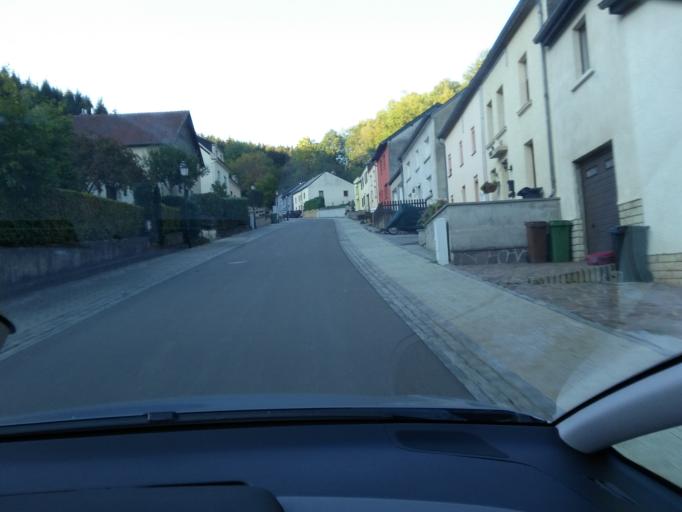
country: LU
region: Luxembourg
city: Eischen
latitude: 49.6826
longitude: 5.8670
